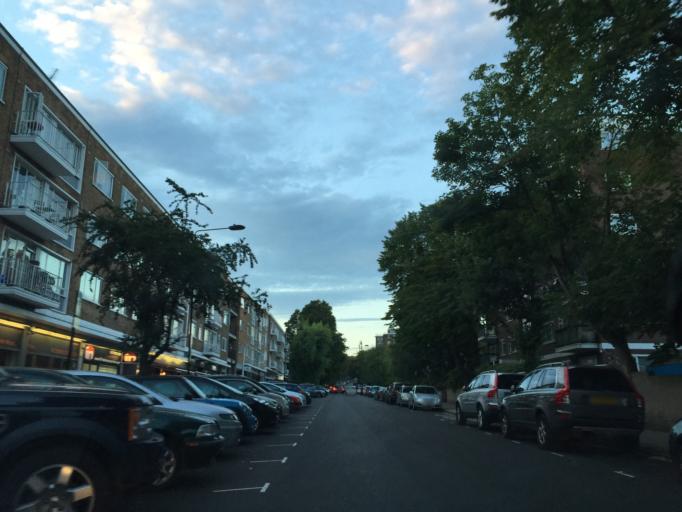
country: GB
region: England
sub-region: Greater London
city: Belsize Park
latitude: 51.5423
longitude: -0.1796
